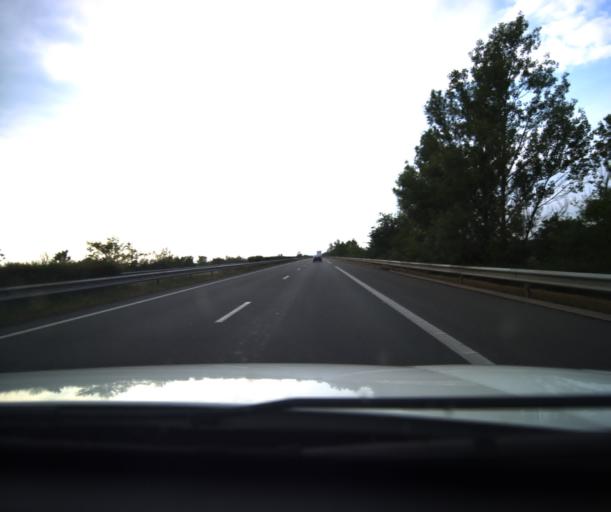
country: FR
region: Midi-Pyrenees
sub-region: Departement du Tarn-et-Garonne
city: Saint-Porquier
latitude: 44.0346
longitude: 1.1578
